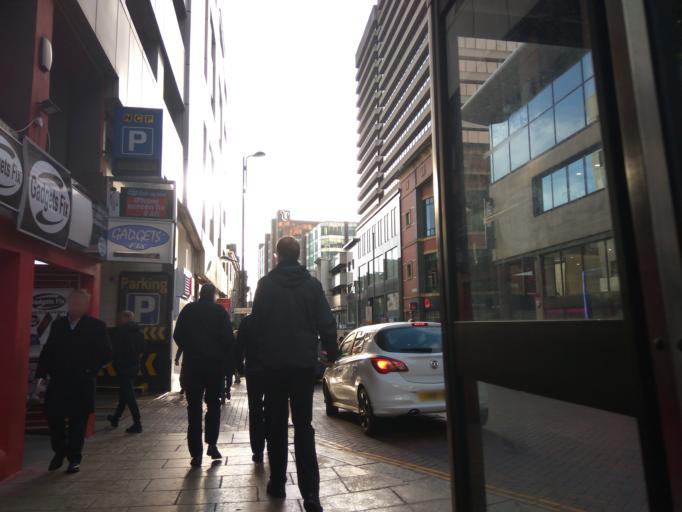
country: GB
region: England
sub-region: City and Borough of Leeds
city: Leeds
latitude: 53.7985
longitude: -1.5451
